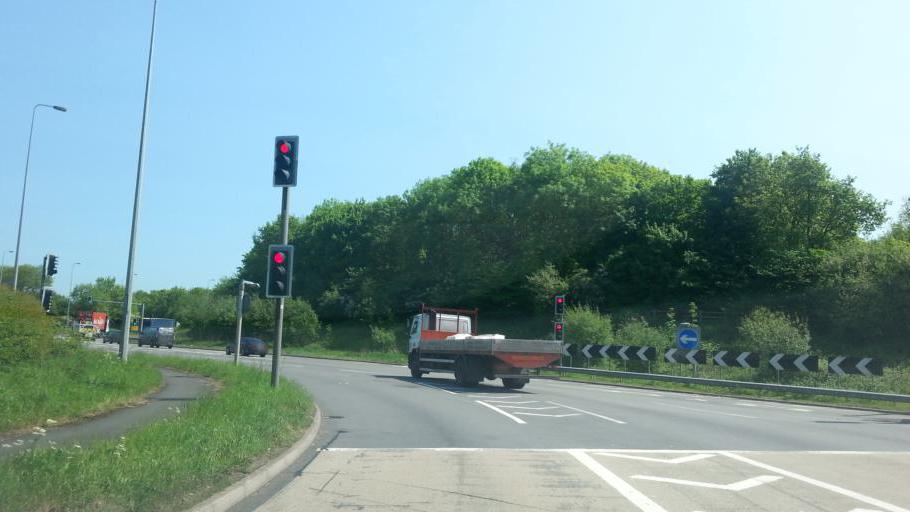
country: GB
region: England
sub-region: Leicestershire
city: Hinckley
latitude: 52.5159
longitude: -1.3629
